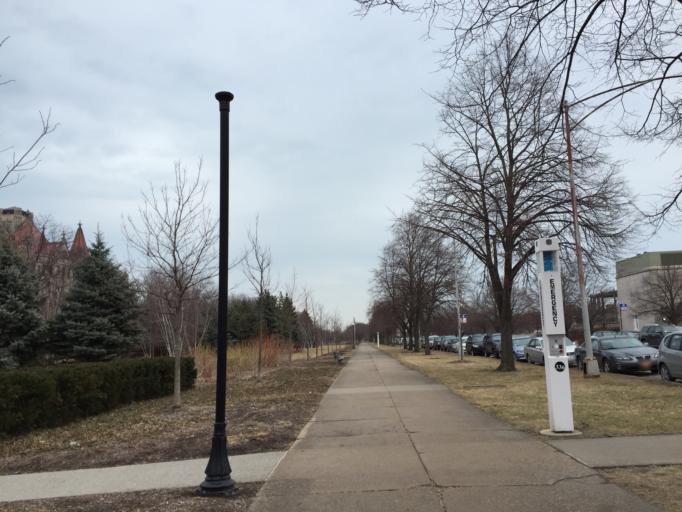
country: US
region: Illinois
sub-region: Cook County
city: Chicago
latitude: 41.7874
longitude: -87.5997
